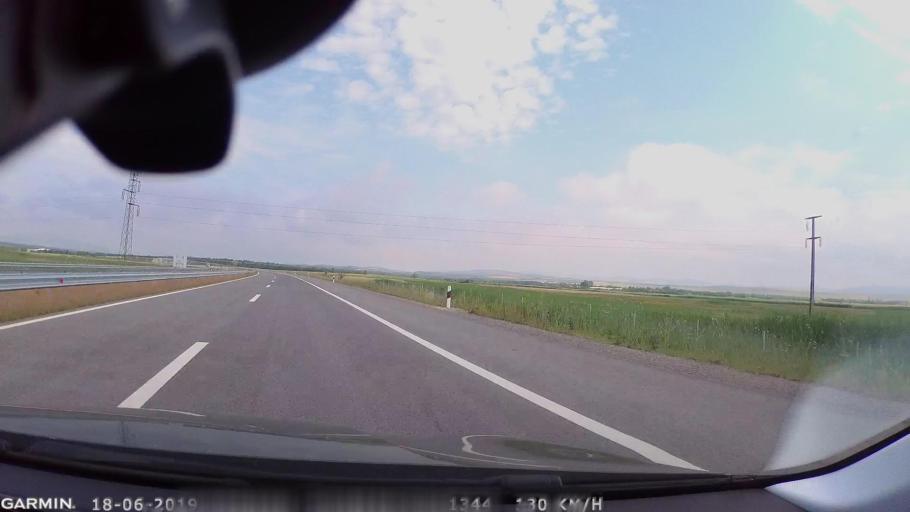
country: MK
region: Sveti Nikole
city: Sveti Nikole
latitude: 41.8211
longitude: 22.0134
